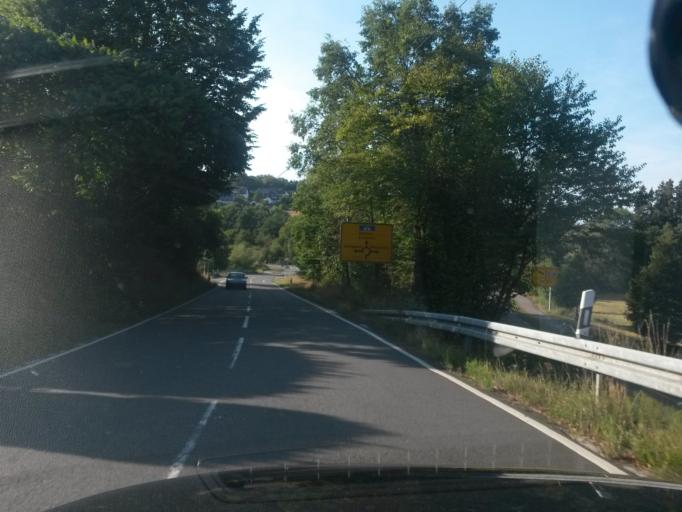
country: DE
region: North Rhine-Westphalia
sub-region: Regierungsbezirk Koln
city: Numbrecht
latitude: 50.9074
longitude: 7.5245
